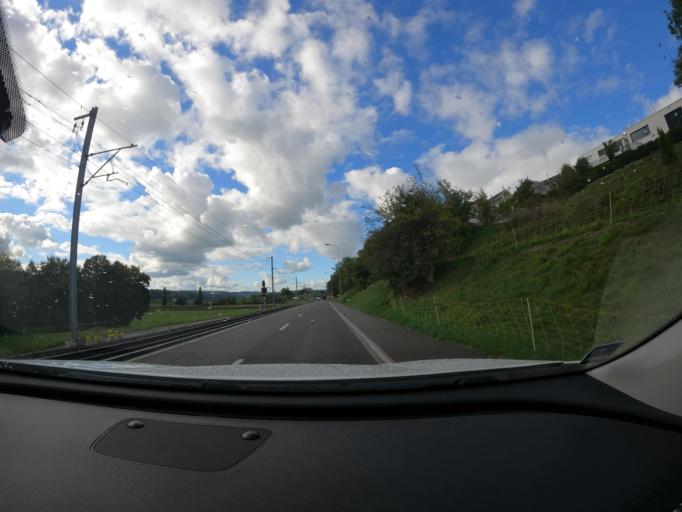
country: CH
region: Aargau
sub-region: Bezirk Kulm
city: Gontenschwil
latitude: 47.2796
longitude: 8.1569
